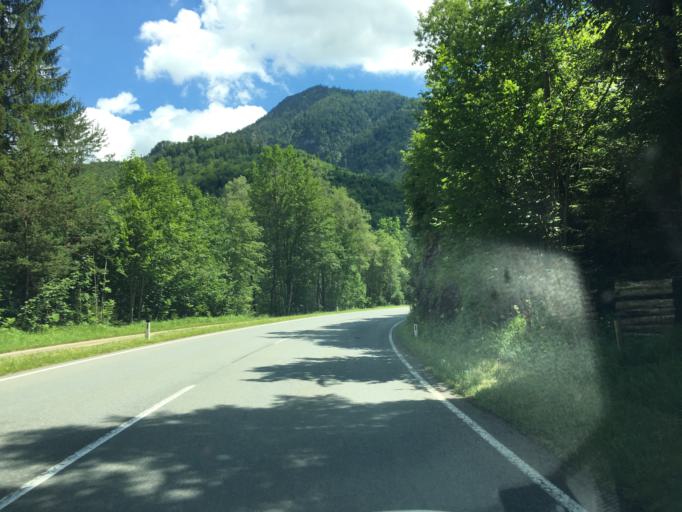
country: AT
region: Salzburg
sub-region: Politischer Bezirk Salzburg-Umgebung
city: Ebenau
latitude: 47.7644
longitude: 13.1791
